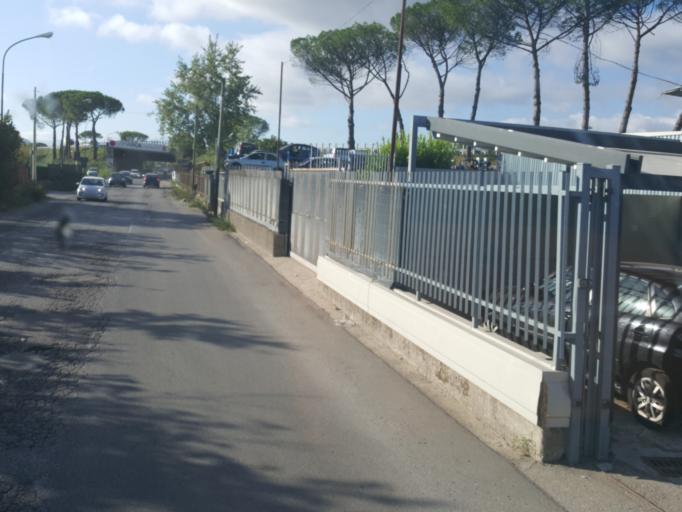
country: IT
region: Campania
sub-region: Provincia di Napoli
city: Nola
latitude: 40.9131
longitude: 14.5269
